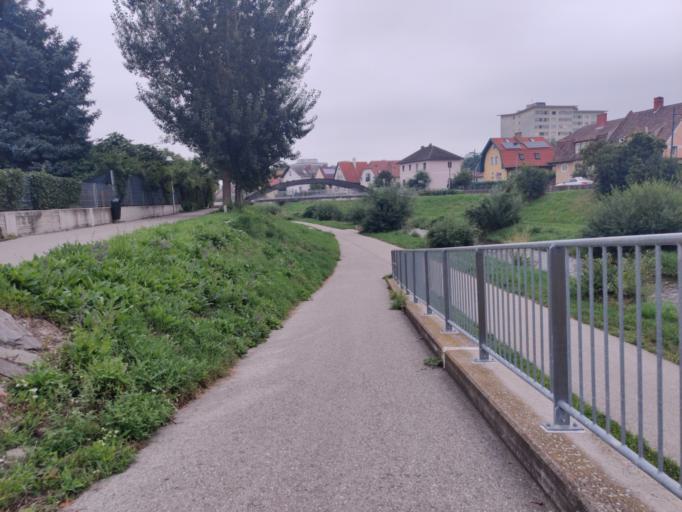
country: AT
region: Lower Austria
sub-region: Krems an der Donau Stadt
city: Krems an der Donau
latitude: 48.4103
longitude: 15.6108
